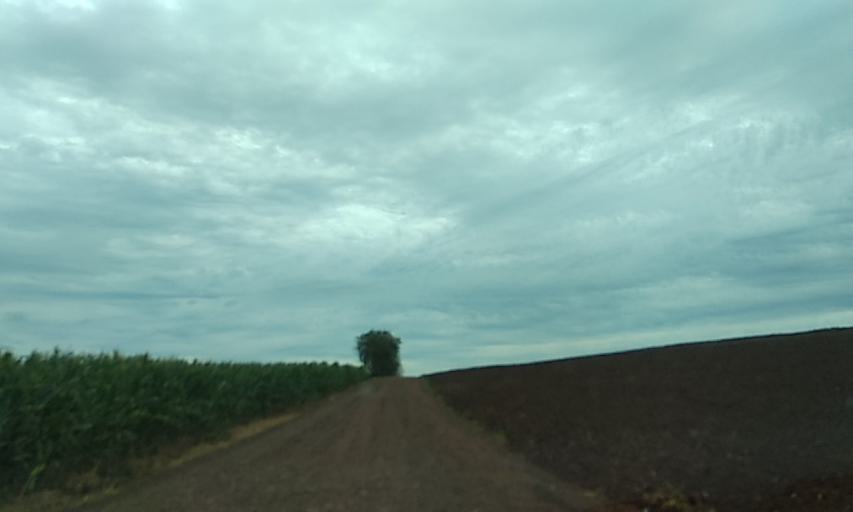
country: BR
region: Parana
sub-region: Marechal Candido Rondon
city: Marechal Candido Rondon
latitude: -24.5272
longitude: -54.0846
